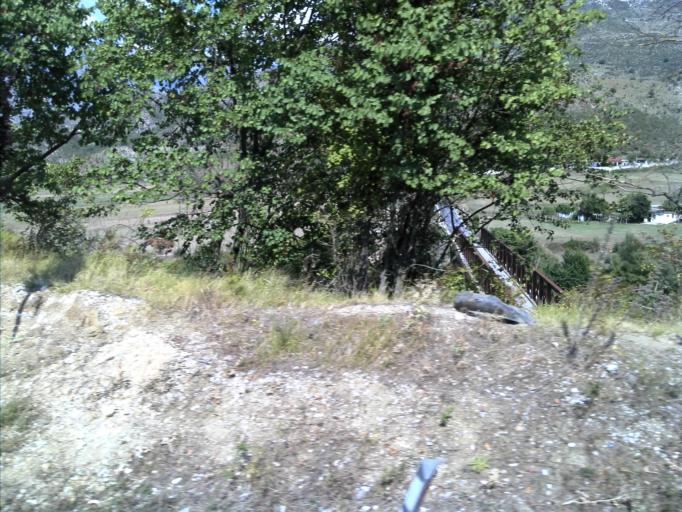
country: AL
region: Gjirokaster
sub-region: Rrethi i Tepelenes
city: Tepelene
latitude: 40.2586
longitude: 20.0544
